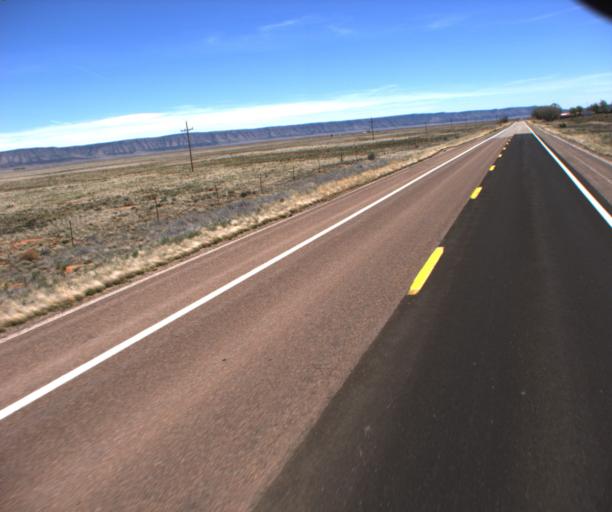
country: US
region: Arizona
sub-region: Mohave County
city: Peach Springs
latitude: 35.4814
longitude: -113.1426
